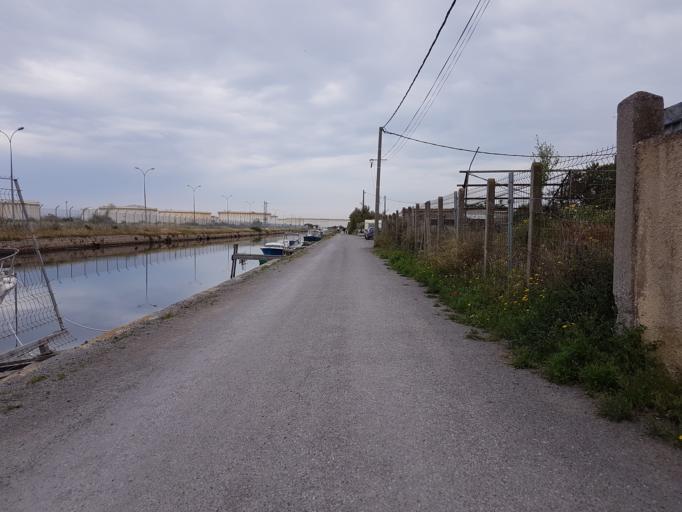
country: FR
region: Languedoc-Roussillon
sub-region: Departement de l'Herault
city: Frontignan
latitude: 43.4395
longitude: 3.7535
